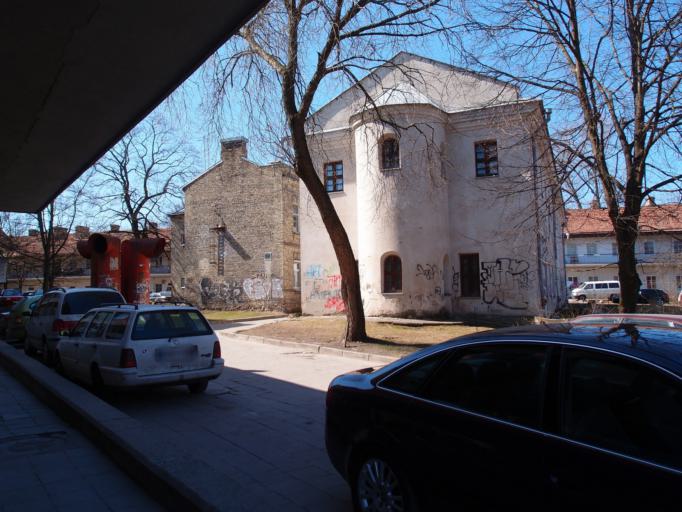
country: LT
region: Vilnius County
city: Rasos
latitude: 54.6820
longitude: 25.2953
